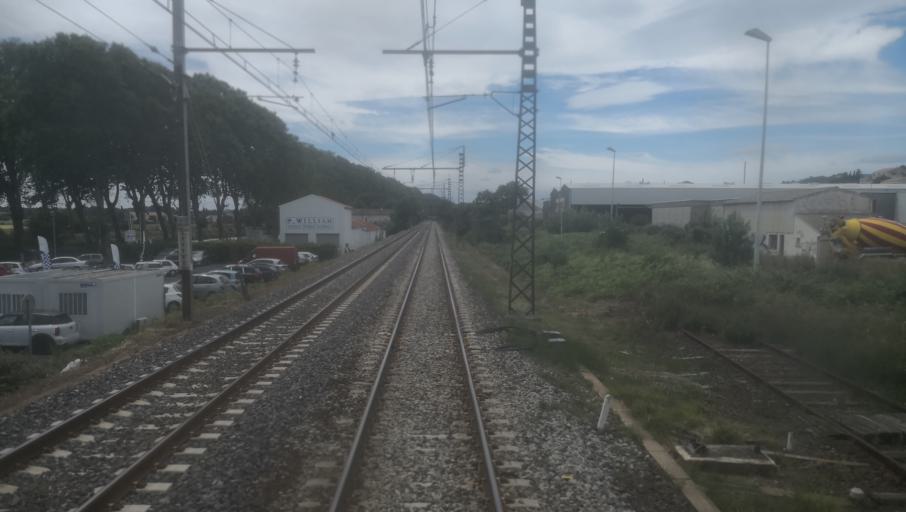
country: FR
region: Languedoc-Roussillon
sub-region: Departement de l'Herault
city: Villeneuve-les-Beziers
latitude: 43.3242
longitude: 3.2594
